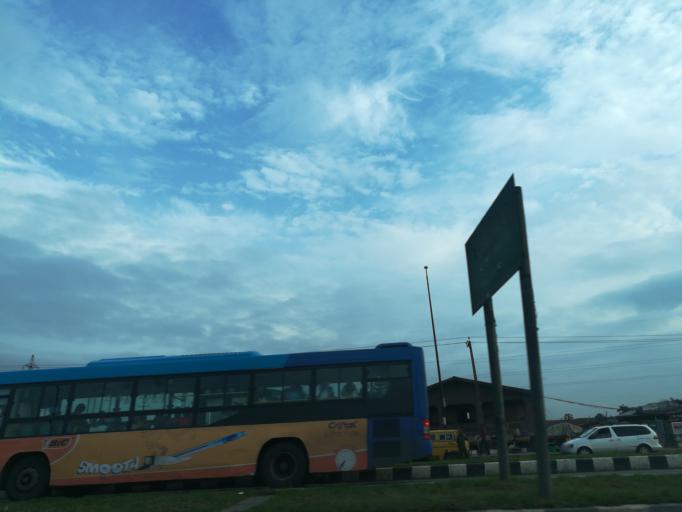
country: NG
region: Lagos
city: Ojota
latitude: 6.6096
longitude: 3.4300
